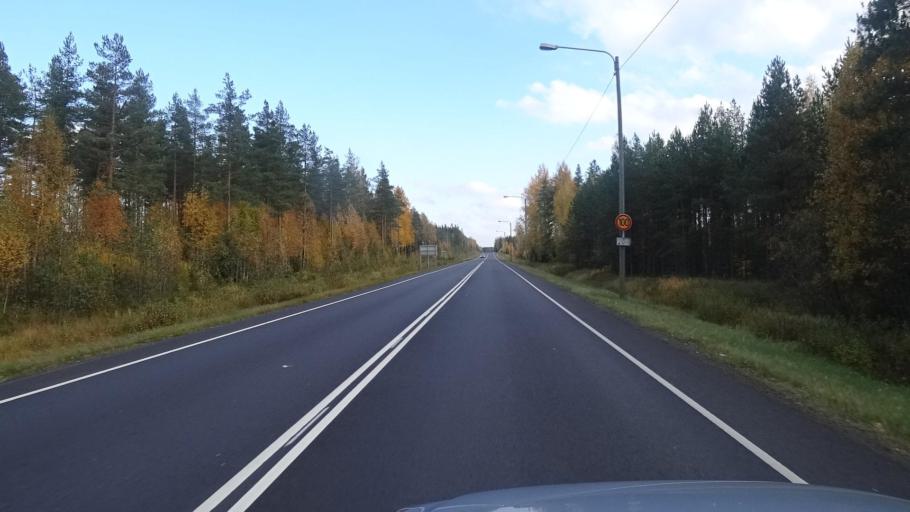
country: FI
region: Satakunta
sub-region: Rauma
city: Eura
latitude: 61.1168
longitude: 22.1911
